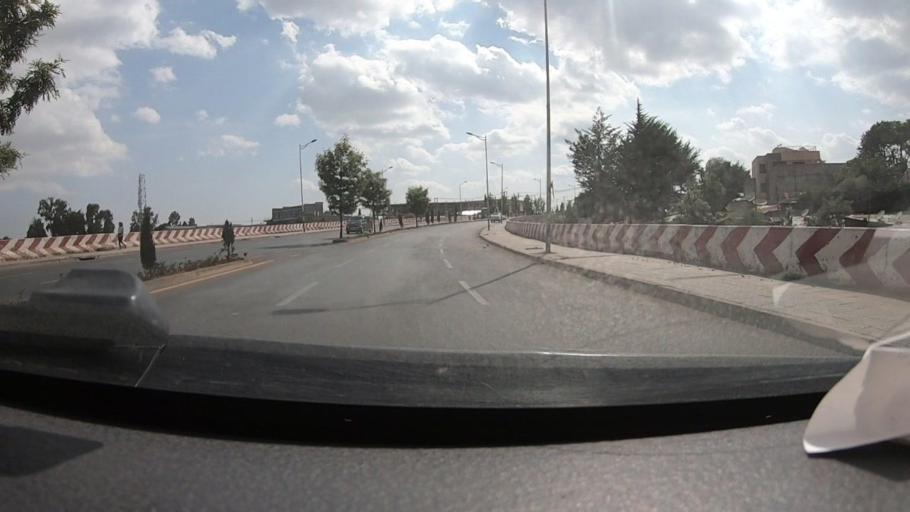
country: ET
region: Adis Abeba
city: Addis Ababa
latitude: 9.0483
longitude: 38.7698
